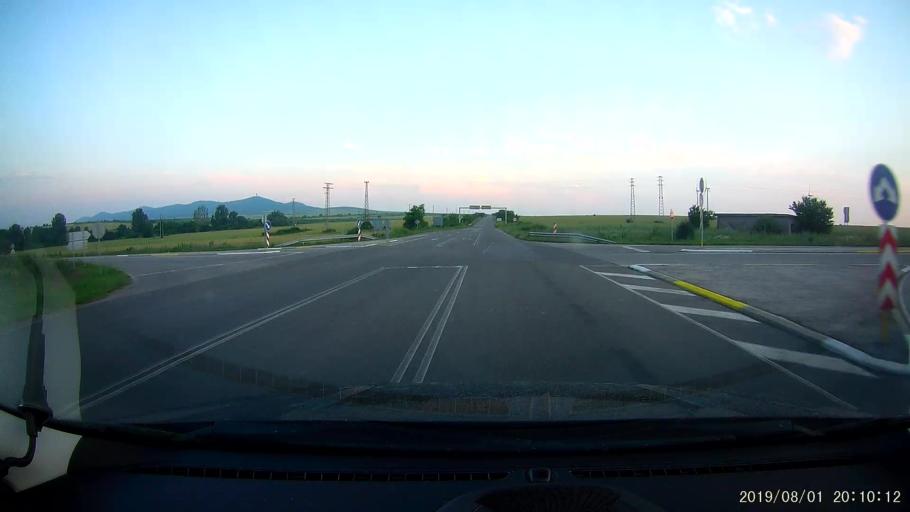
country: BG
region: Yambol
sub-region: Obshtina Yambol
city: Yambol
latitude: 42.4856
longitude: 26.5972
